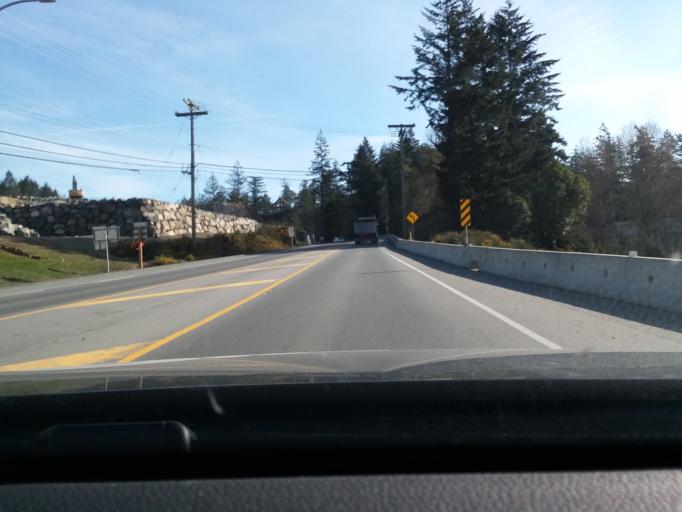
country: CA
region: British Columbia
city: Metchosin
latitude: 48.4263
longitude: -123.5461
